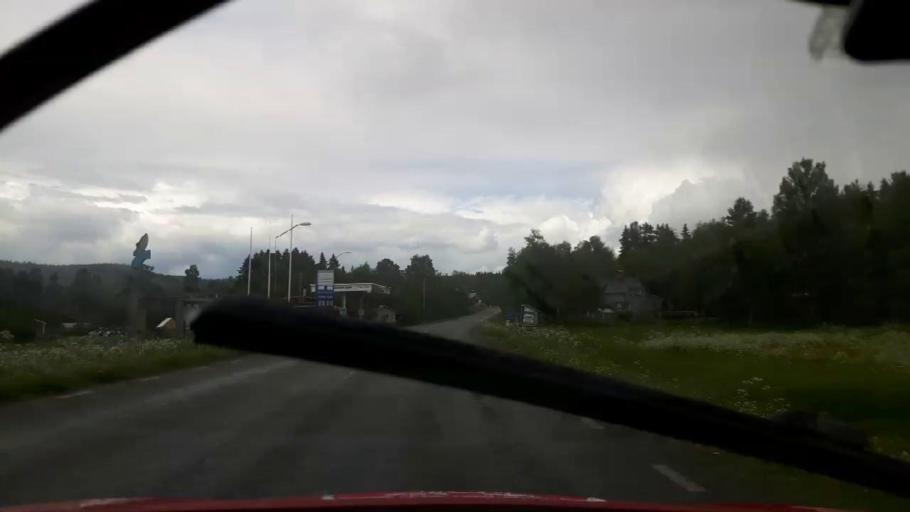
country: SE
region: Jaemtland
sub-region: Krokoms Kommun
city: Krokom
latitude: 63.4542
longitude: 14.1909
